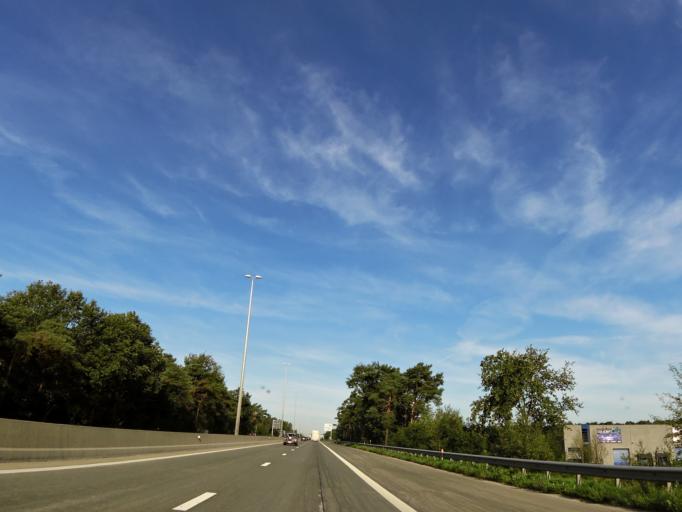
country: BE
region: Flanders
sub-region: Provincie Antwerpen
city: Vorselaar
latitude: 51.1663
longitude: 4.7858
